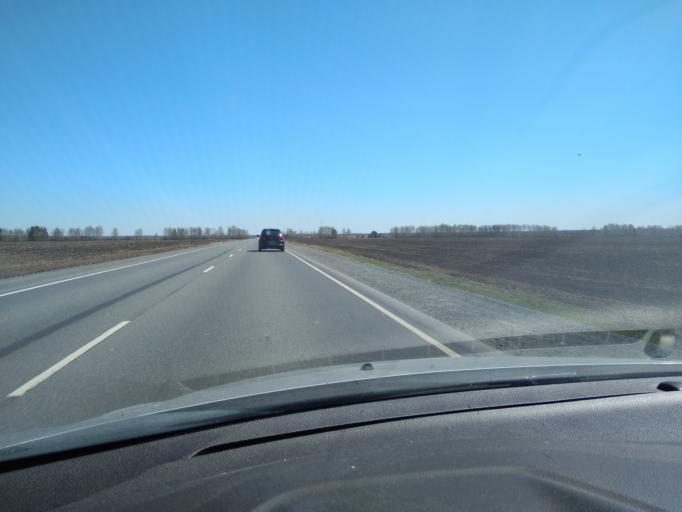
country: RU
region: Sverdlovsk
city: Tugulym
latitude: 57.0754
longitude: 64.7993
